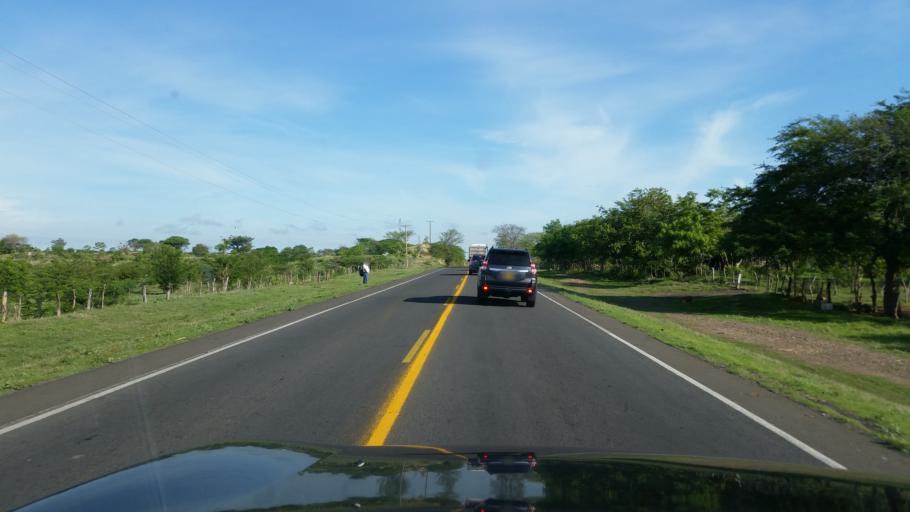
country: NI
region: Leon
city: La Paz Centro
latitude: 12.2294
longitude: -86.7017
